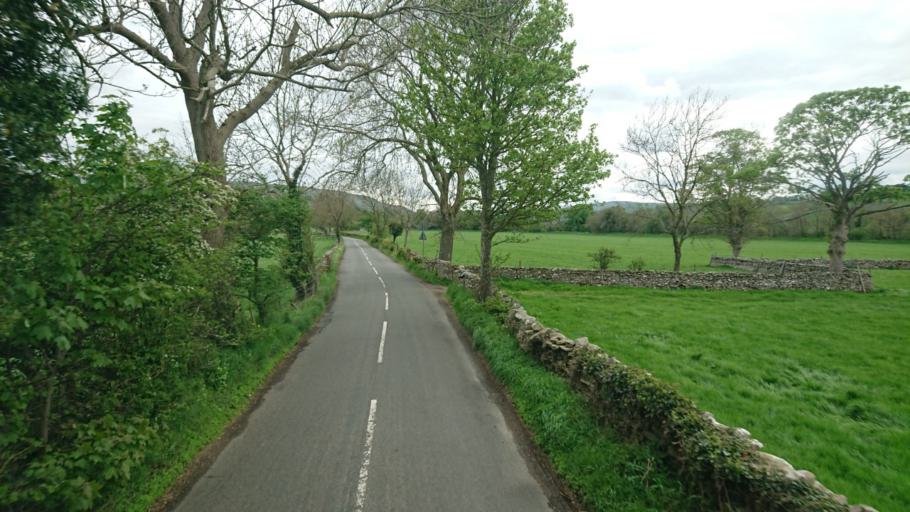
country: GB
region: England
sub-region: North Yorkshire
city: Leyburn
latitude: 54.2879
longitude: -1.9677
